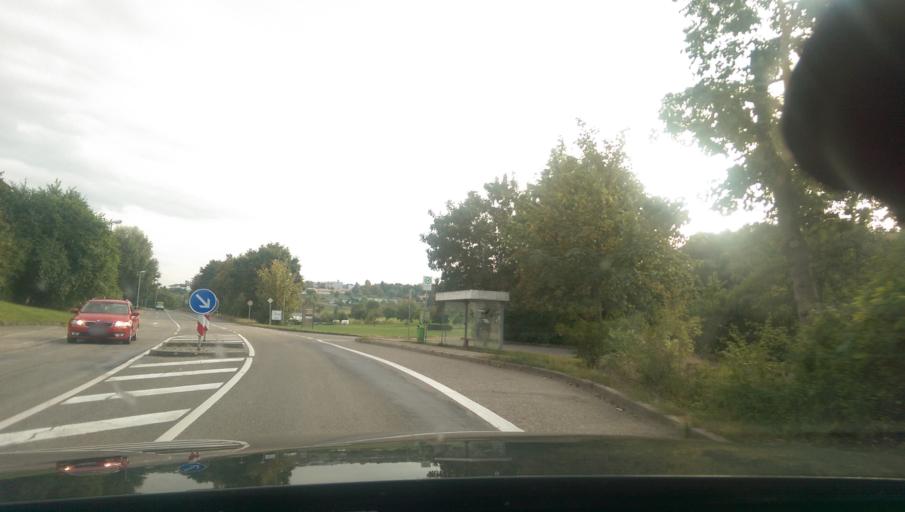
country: DE
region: Baden-Wuerttemberg
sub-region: Karlsruhe Region
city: Heimsheim
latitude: 48.8144
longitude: 8.8620
